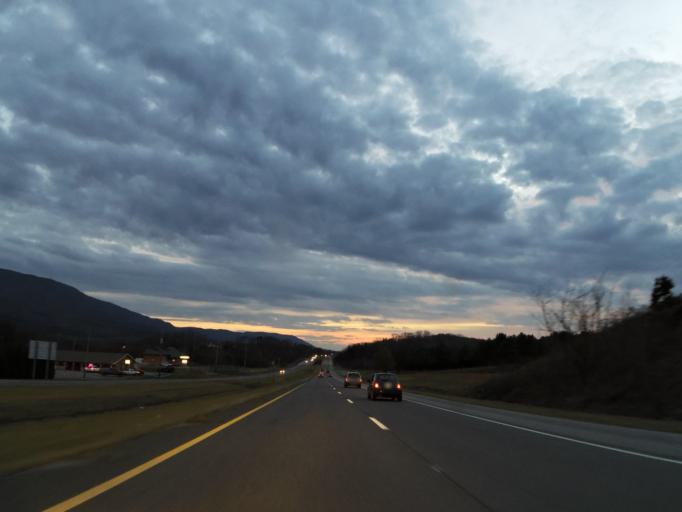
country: US
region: Tennessee
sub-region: McMinn County
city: Etowah
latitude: 35.2452
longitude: -84.5605
